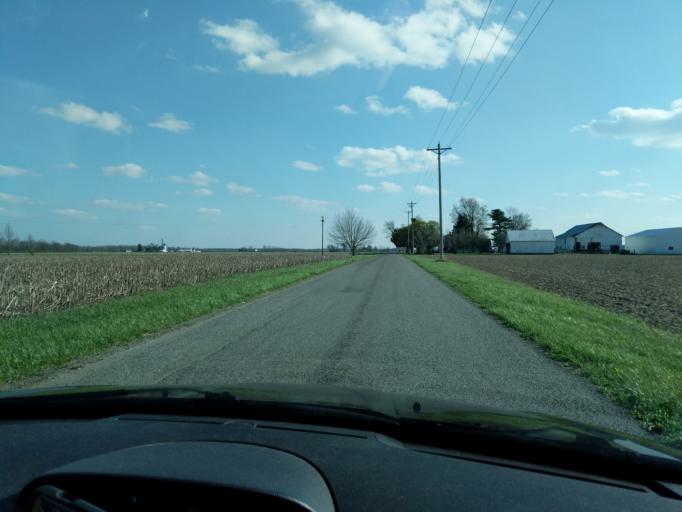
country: US
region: Ohio
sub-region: Champaign County
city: Urbana
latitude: 40.1207
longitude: -83.8080
